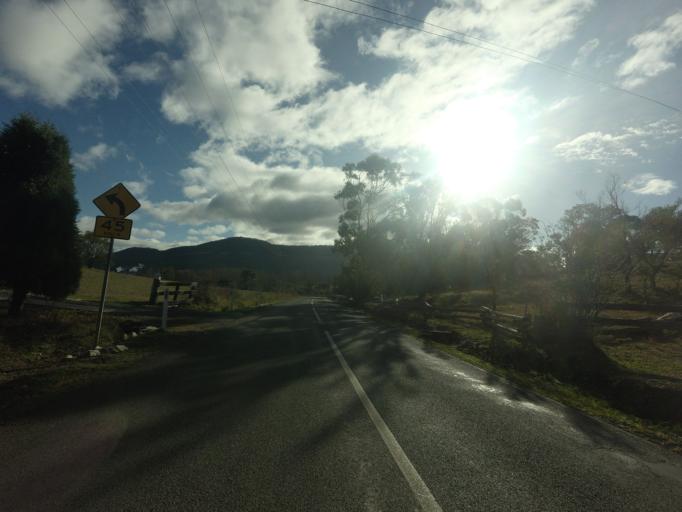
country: AU
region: Tasmania
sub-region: Derwent Valley
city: New Norfolk
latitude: -42.7848
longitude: 147.1175
